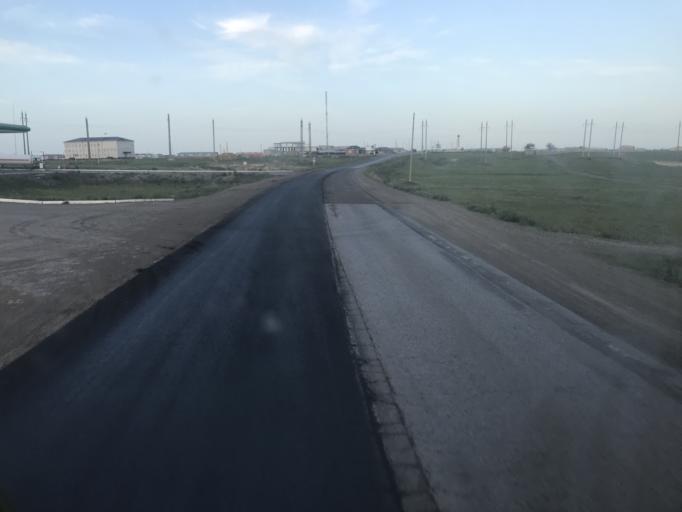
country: KZ
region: Aqtoebe
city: Khromtau
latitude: 50.2594
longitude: 58.4050
